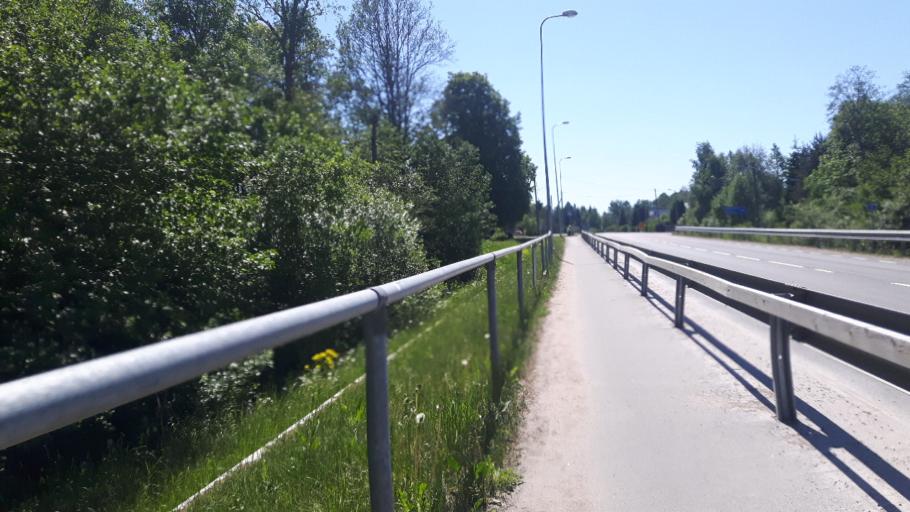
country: EE
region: Harju
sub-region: Saku vald
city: Saku
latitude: 59.2329
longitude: 24.6814
